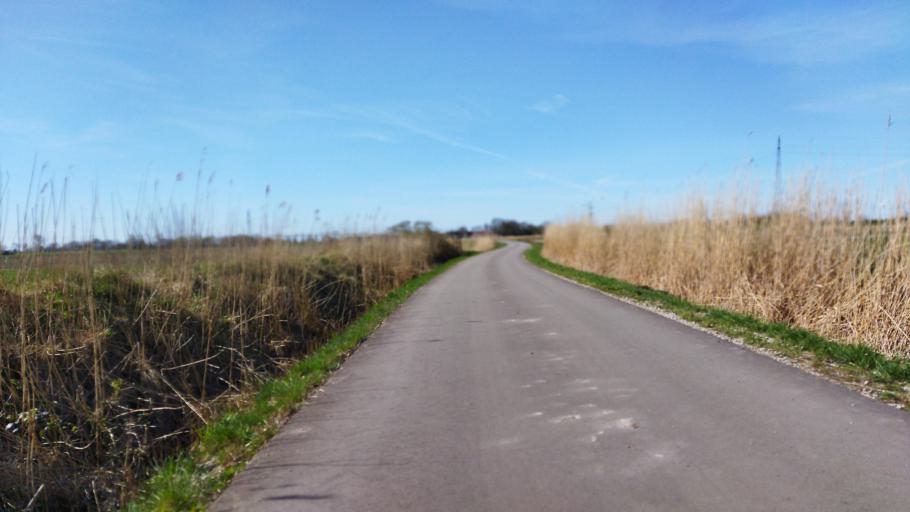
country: DE
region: Lower Saxony
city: Elsfleth
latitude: 53.2168
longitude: 8.4598
